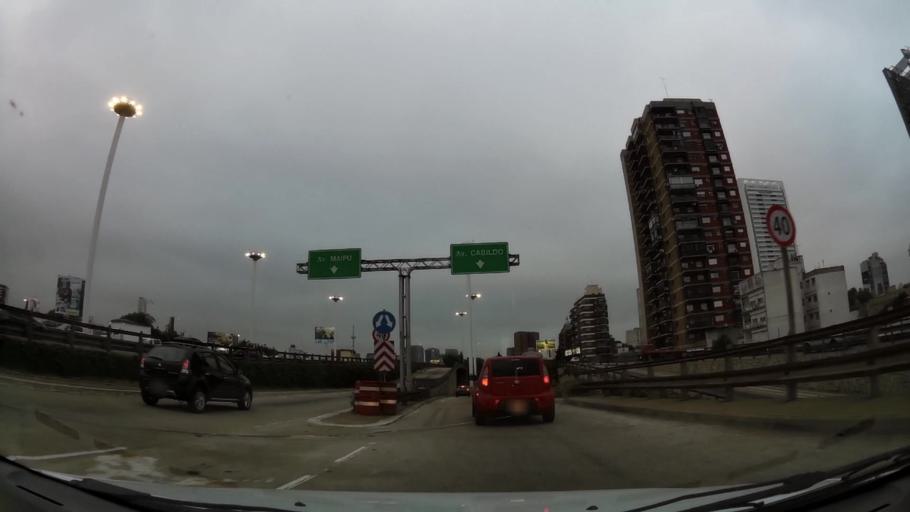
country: AR
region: Buenos Aires
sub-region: Partido de Vicente Lopez
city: Olivos
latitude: -34.5397
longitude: -58.4770
